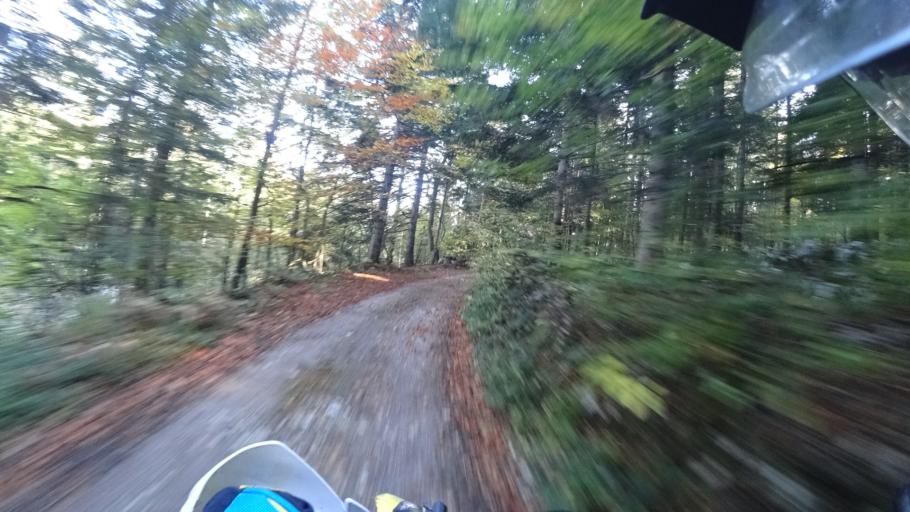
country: HR
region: Karlovacka
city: Plaski
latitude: 45.0121
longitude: 15.4016
